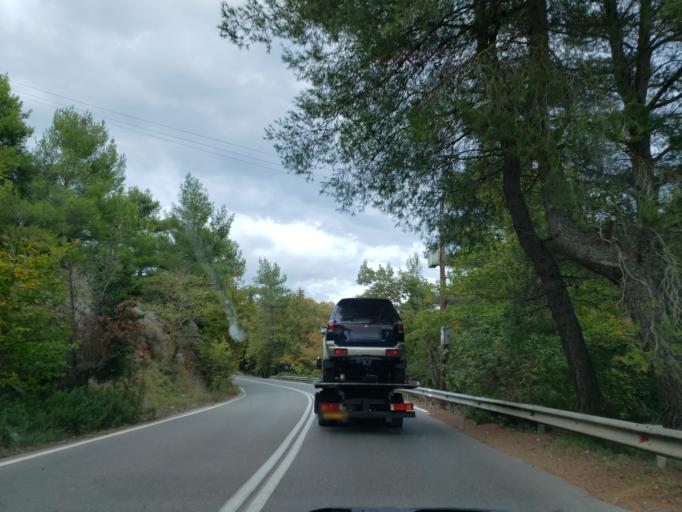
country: GR
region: Attica
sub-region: Nomarchia Anatolikis Attikis
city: Varnavas
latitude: 38.2151
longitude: 23.9131
